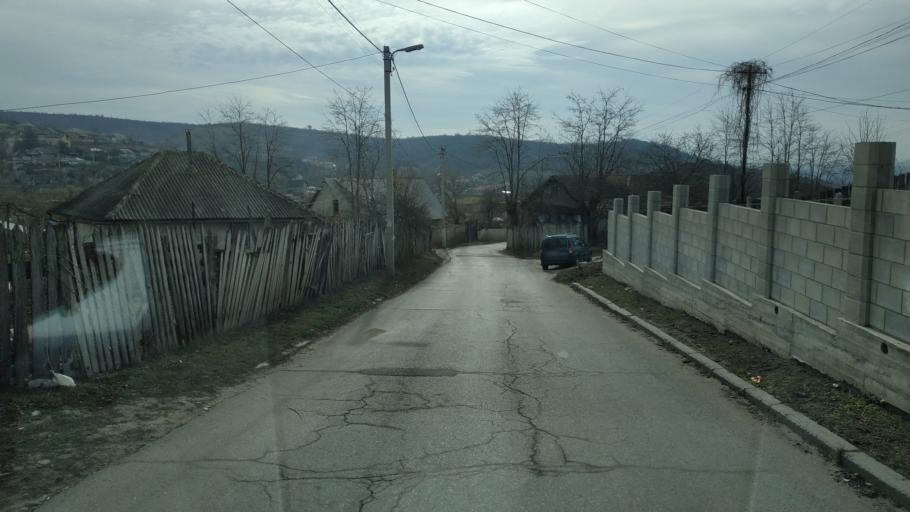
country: MD
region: Chisinau
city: Vatra
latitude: 47.0925
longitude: 28.7681
